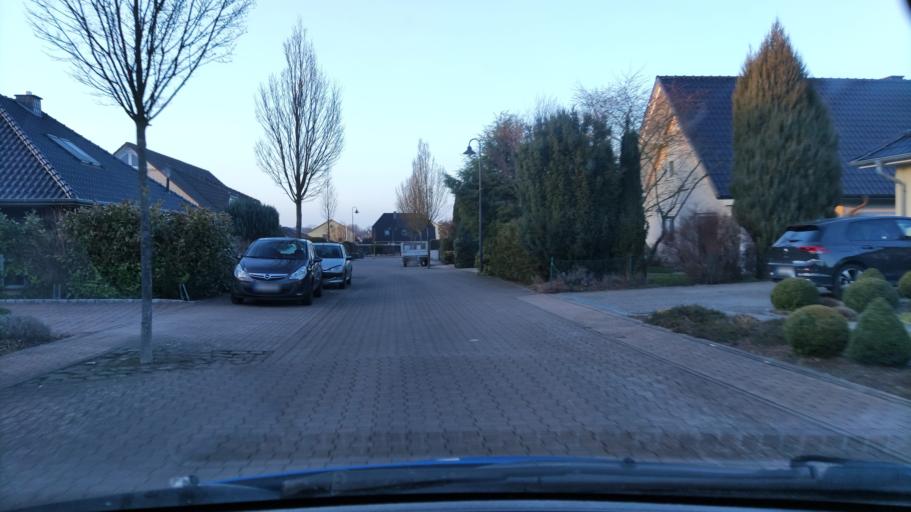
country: DE
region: Lower Saxony
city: Ebstorf
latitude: 53.0217
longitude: 10.4116
